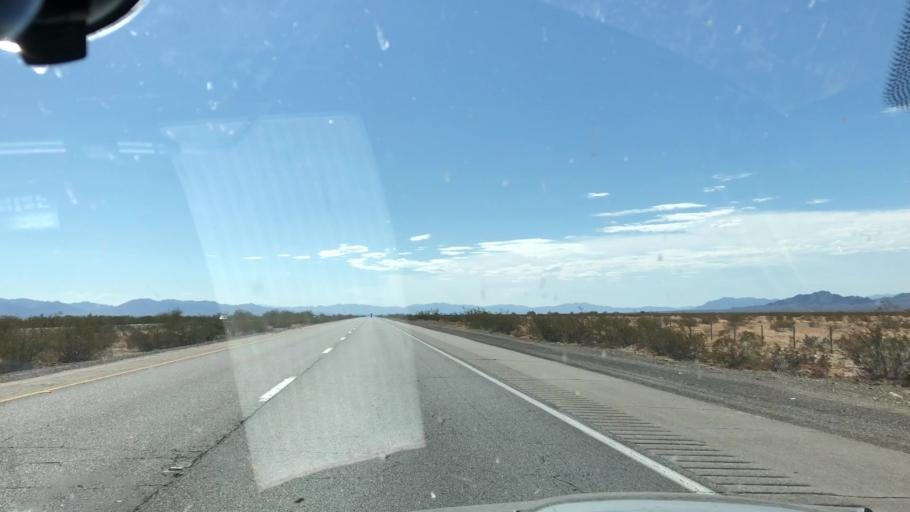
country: US
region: California
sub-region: Riverside County
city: Mesa Verde
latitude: 33.6125
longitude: -115.0065
